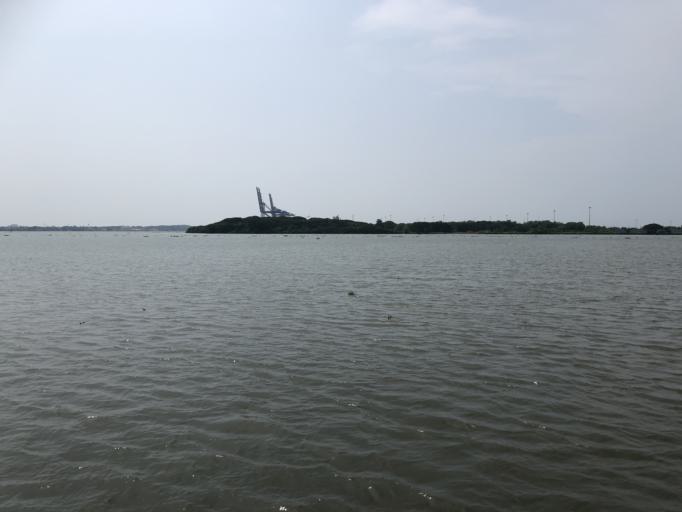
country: IN
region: Kerala
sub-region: Ernakulam
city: Cochin
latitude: 9.9853
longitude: 76.2642
